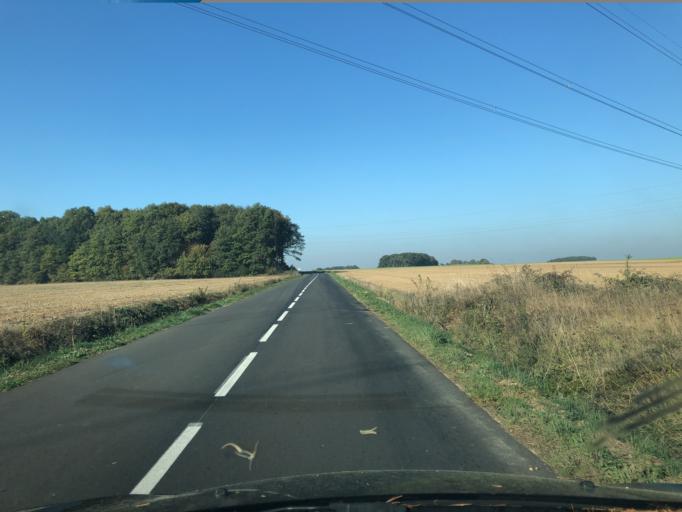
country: FR
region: Centre
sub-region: Departement d'Indre-et-Loire
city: Rouziers-de-Touraine
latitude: 47.5340
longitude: 0.6384
